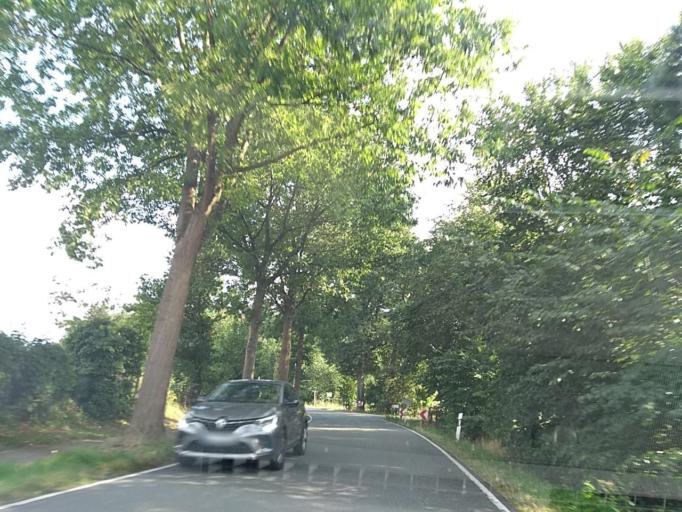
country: DE
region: North Rhine-Westphalia
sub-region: Regierungsbezirk Detmold
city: Verl
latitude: 51.9499
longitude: 8.5250
